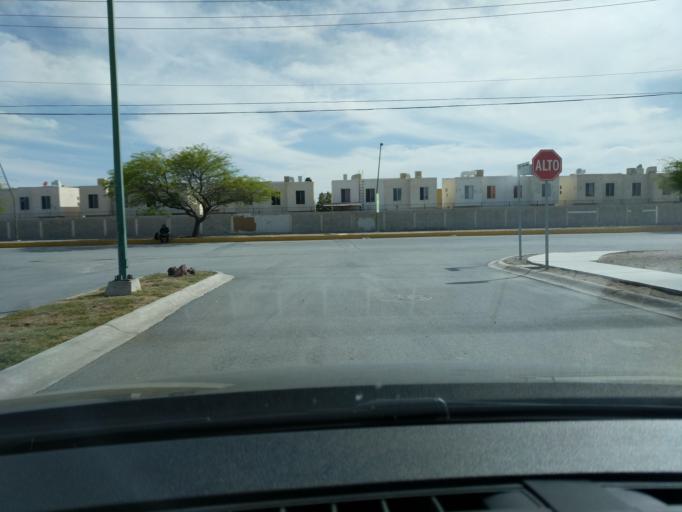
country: MX
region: Coahuila
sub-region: Torreon
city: Fraccionamiento la Noria
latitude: 25.5203
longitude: -103.3152
